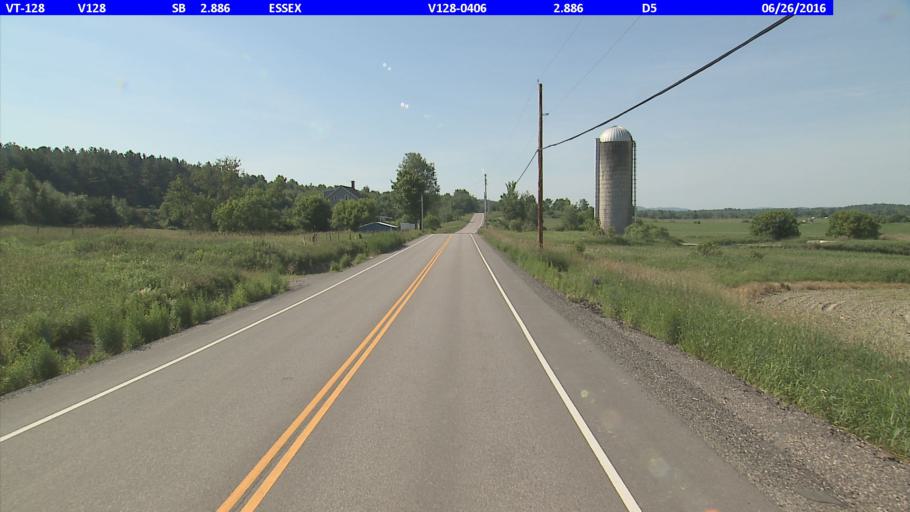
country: US
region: Vermont
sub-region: Chittenden County
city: Jericho
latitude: 44.5392
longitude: -73.0321
